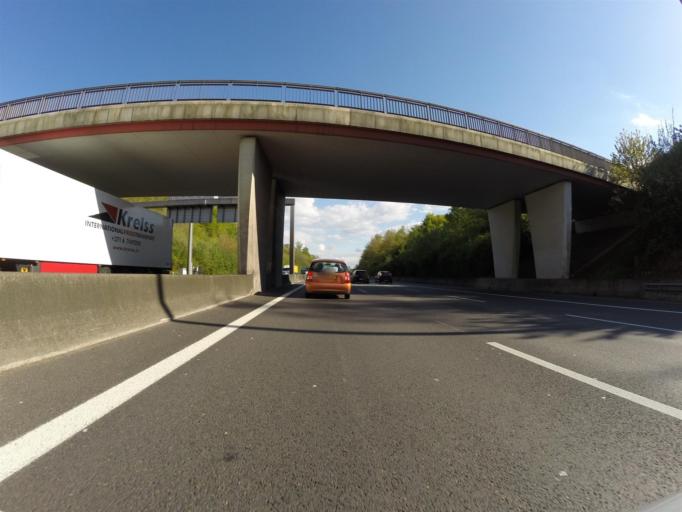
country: LU
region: Luxembourg
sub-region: Canton de Luxembourg
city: Hesperange
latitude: 49.5662
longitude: 6.1281
